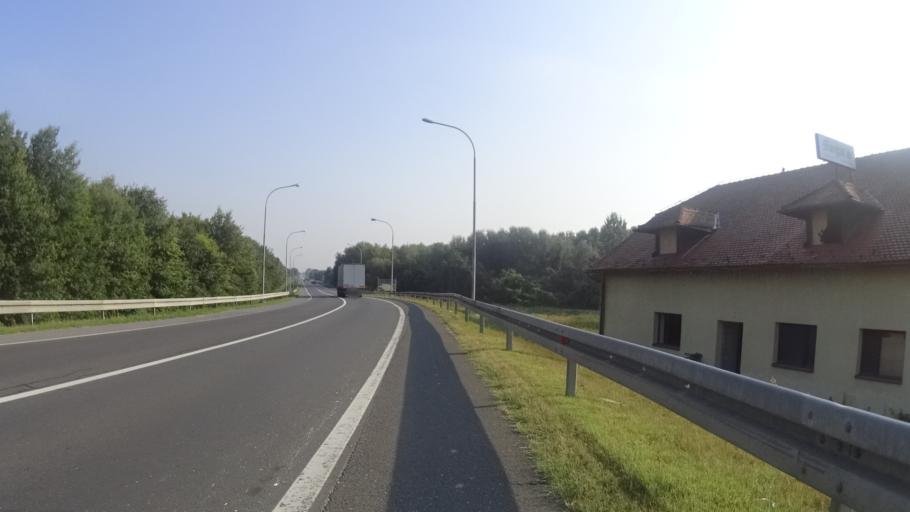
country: HR
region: Varazdinska
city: Varazdin
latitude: 46.3232
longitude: 16.3588
